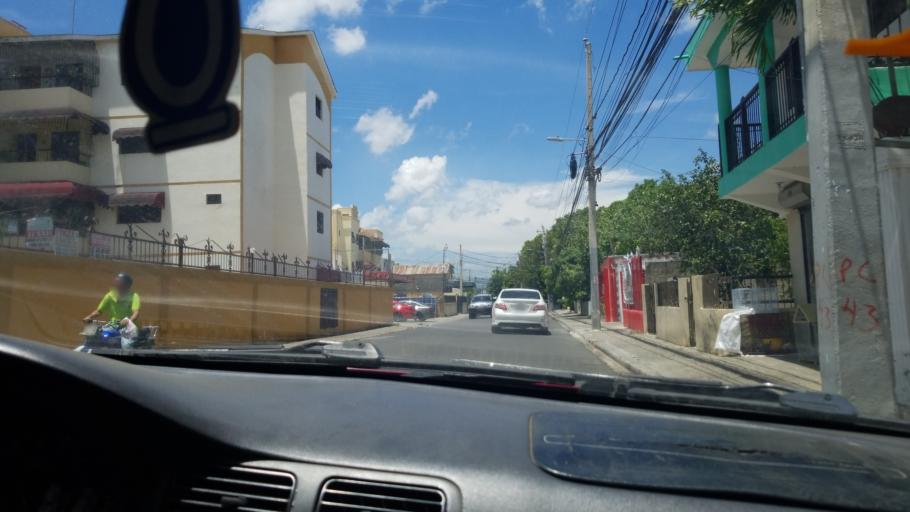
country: DO
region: Santiago
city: Santiago de los Caballeros
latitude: 19.4749
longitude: -70.6903
